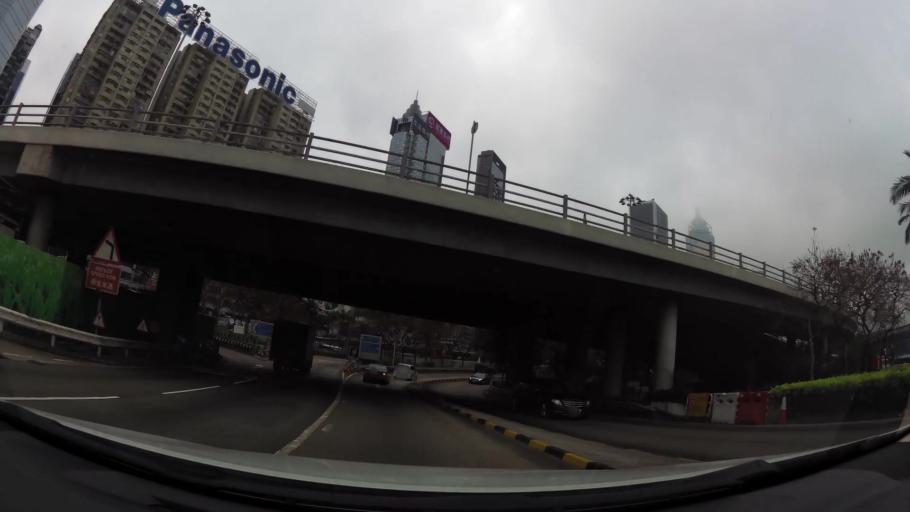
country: HK
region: Wanchai
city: Wan Chai
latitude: 22.2823
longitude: 114.1816
